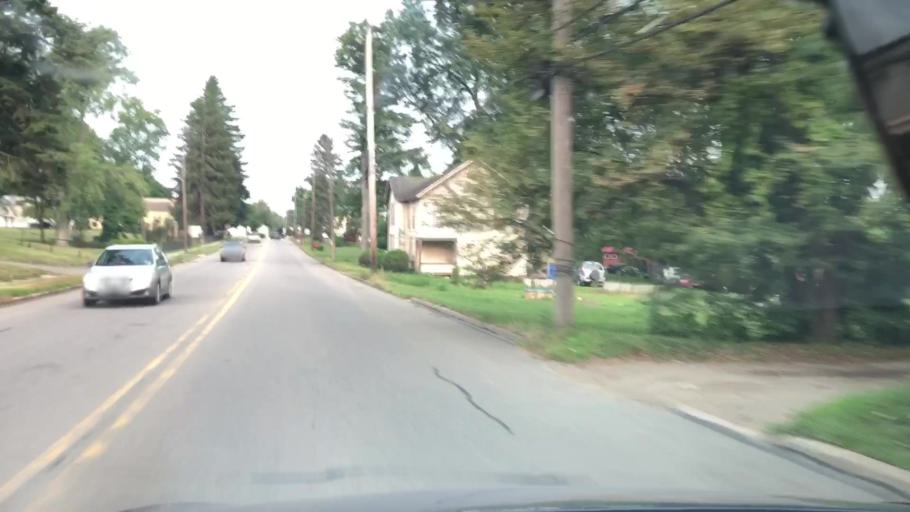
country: US
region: Pennsylvania
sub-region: Crawford County
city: Titusville
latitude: 41.6322
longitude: -79.6922
